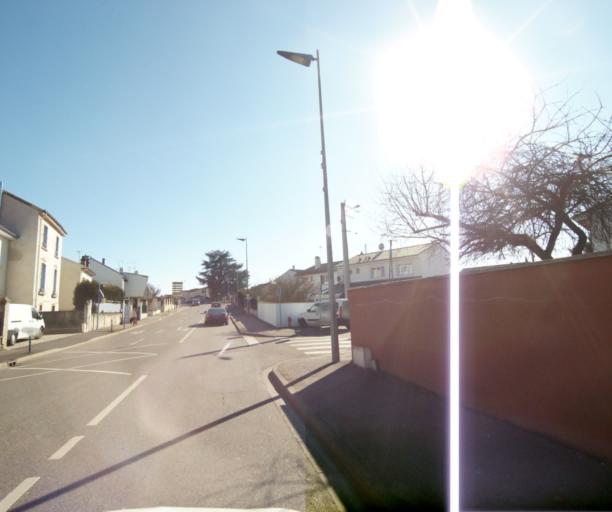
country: FR
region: Lorraine
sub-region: Departement de Meurthe-et-Moselle
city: Tomblaine
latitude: 48.6811
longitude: 6.2161
